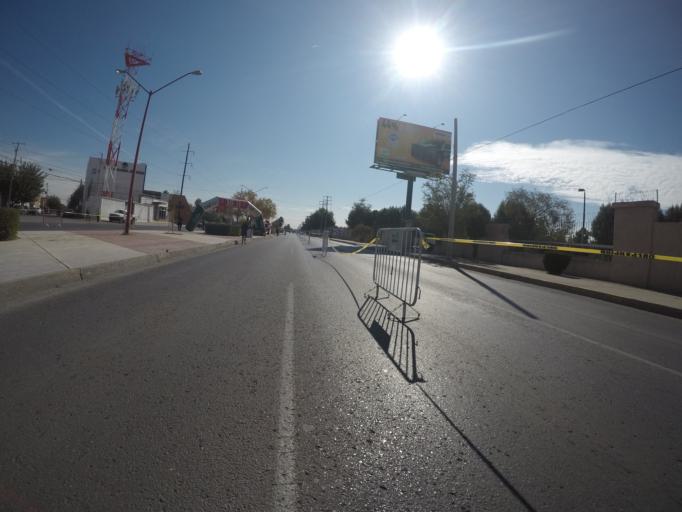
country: MX
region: Chihuahua
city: Ciudad Juarez
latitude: 31.7286
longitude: -106.4076
